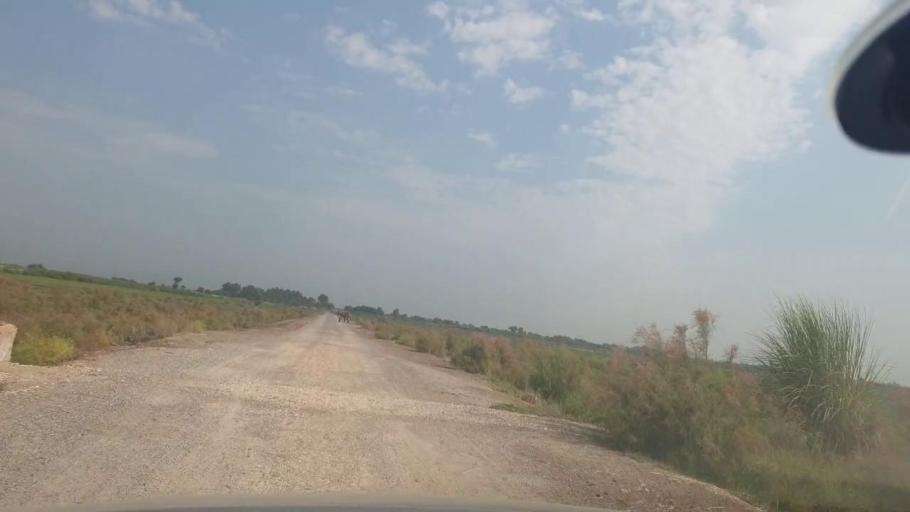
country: PK
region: Balochistan
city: Mehrabpur
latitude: 28.0459
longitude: 68.1221
